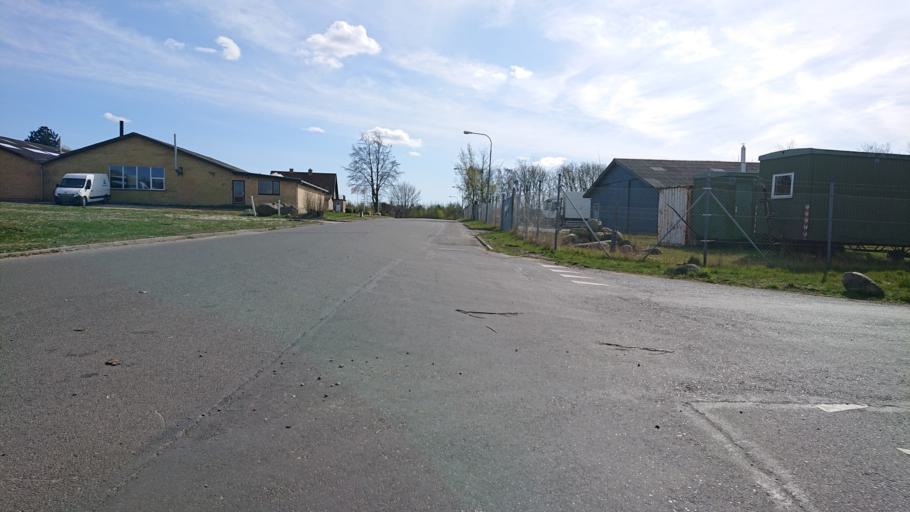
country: DK
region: South Denmark
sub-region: Nyborg Kommune
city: Nyborg
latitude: 55.3116
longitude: 10.7516
